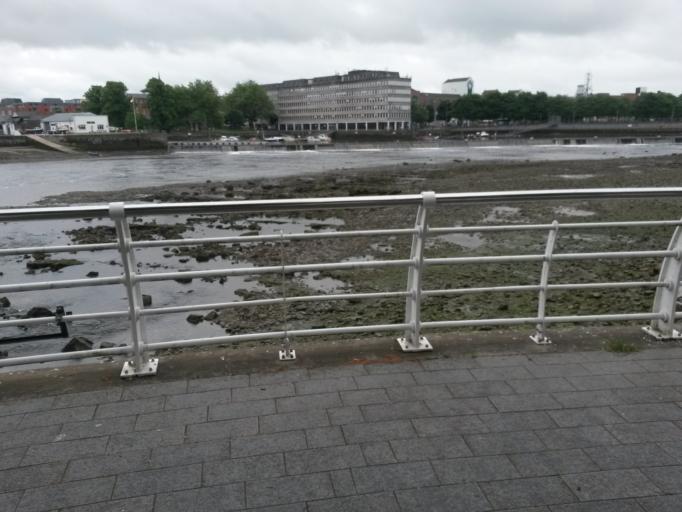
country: IE
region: Munster
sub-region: County Limerick
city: Luimneach
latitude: 52.6681
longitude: -8.6275
